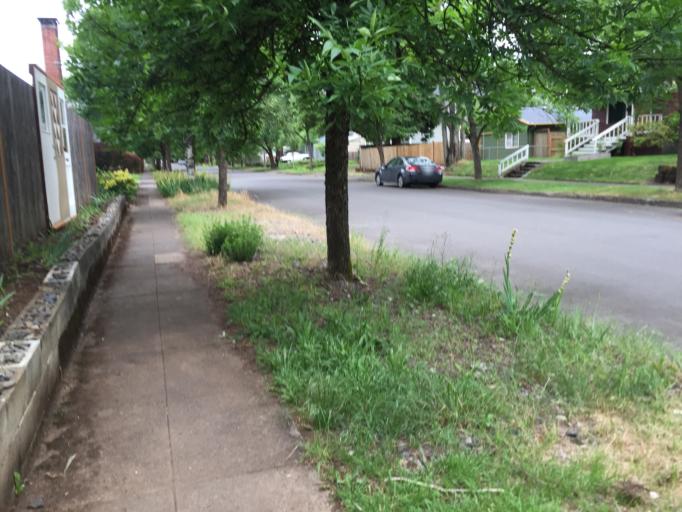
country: US
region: Oregon
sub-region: Multnomah County
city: Lents
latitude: 45.4919
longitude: -122.6114
